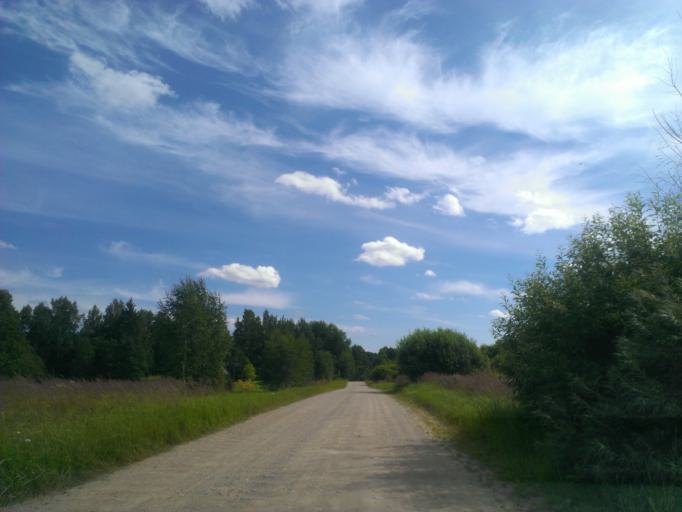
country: LV
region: Ligatne
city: Ligatne
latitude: 57.2175
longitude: 25.0100
